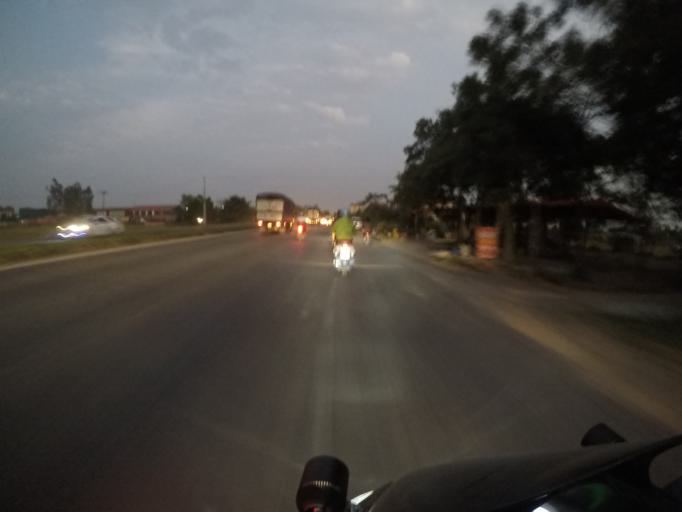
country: VN
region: Vinh Phuc
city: Phuc Yen
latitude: 21.2324
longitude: 105.7527
